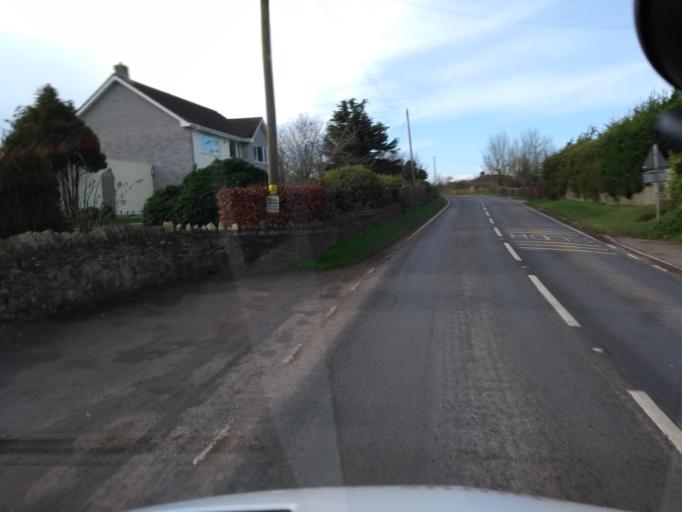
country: GB
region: England
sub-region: Somerset
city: Westonzoyland
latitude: 51.0551
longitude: -2.9543
